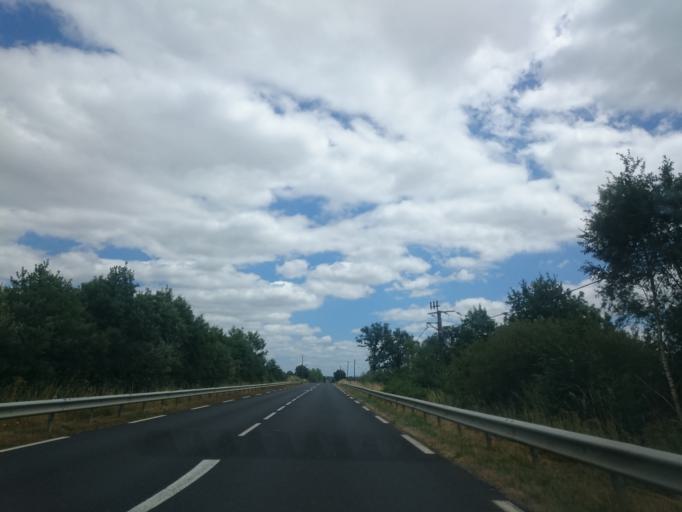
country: FR
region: Auvergne
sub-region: Departement du Cantal
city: Saint-Paul-des-Landes
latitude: 44.9513
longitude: 2.2914
